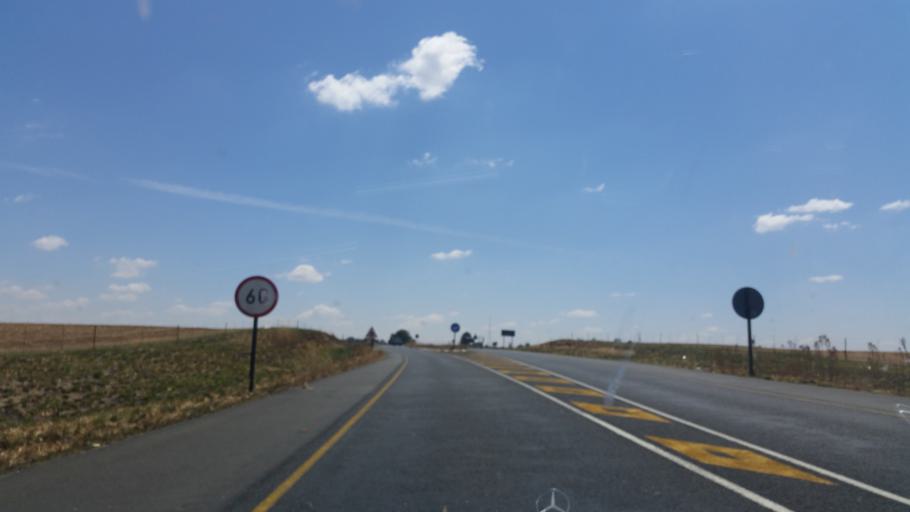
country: ZA
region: Orange Free State
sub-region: Thabo Mofutsanyana District Municipality
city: Reitz
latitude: -28.0848
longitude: 28.6507
